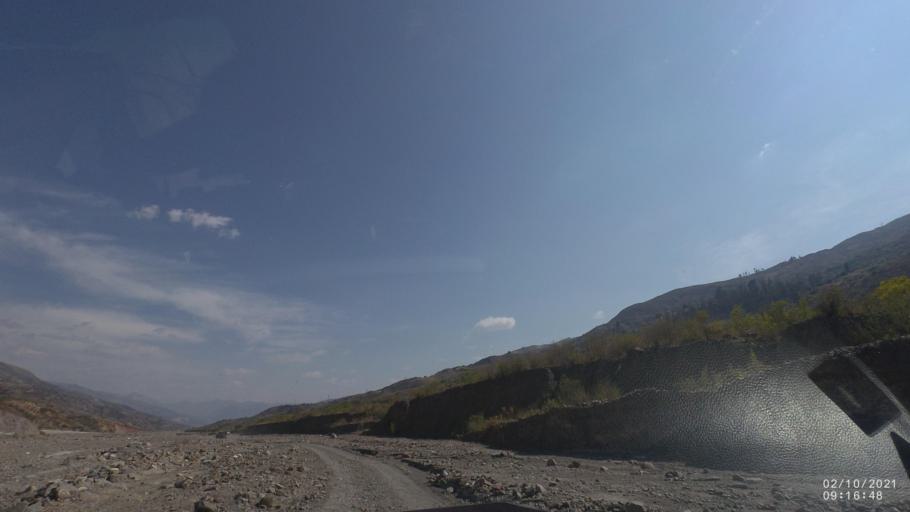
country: BO
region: Cochabamba
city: Irpa Irpa
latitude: -17.8822
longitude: -66.3046
